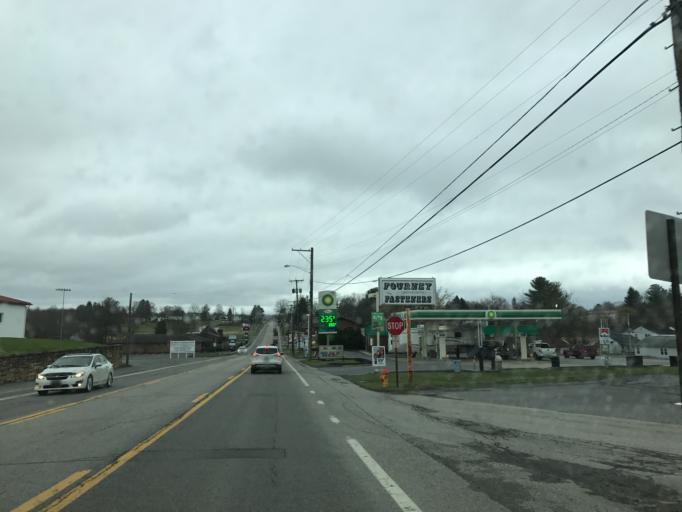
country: US
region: West Virginia
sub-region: Raleigh County
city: Beckley
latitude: 37.7810
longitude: -81.1672
